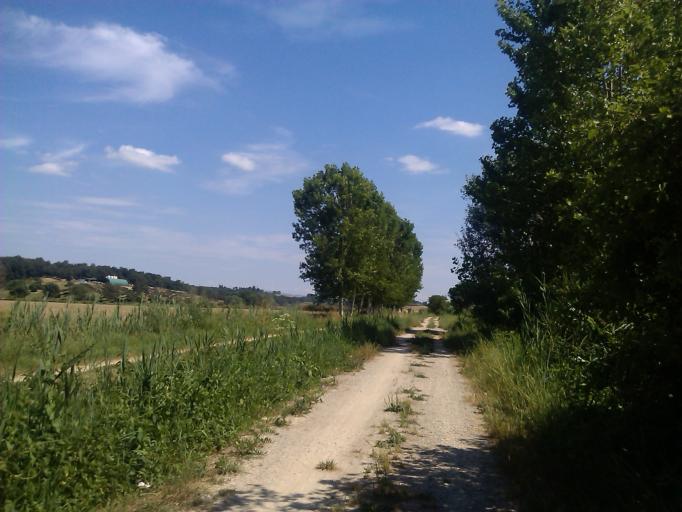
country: IT
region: Umbria
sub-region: Provincia di Perugia
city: Pozzuolo
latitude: 43.0717
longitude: 11.9260
